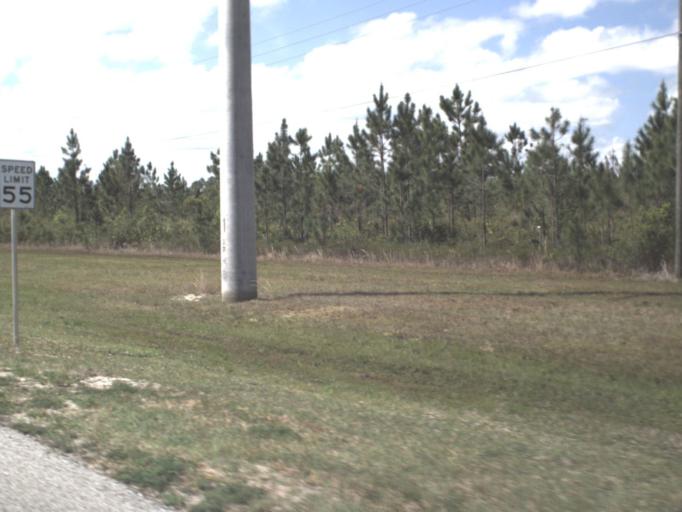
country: US
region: Florida
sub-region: Flagler County
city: Bunnell
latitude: 29.5001
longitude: -81.2649
